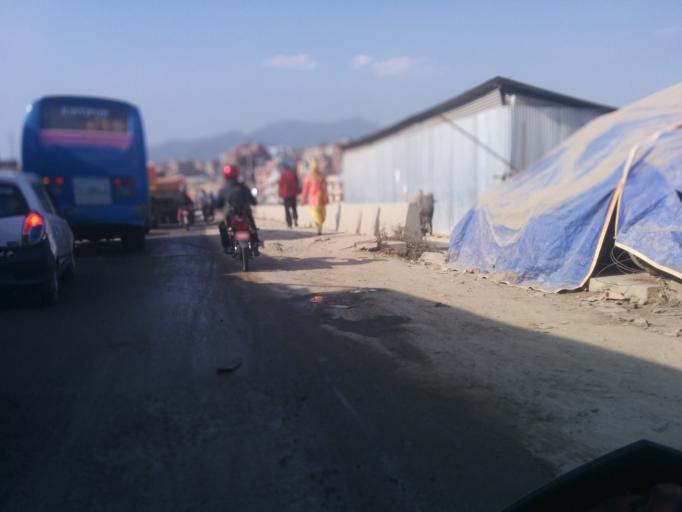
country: NP
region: Central Region
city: Kirtipur
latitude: 27.6896
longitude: 85.2840
